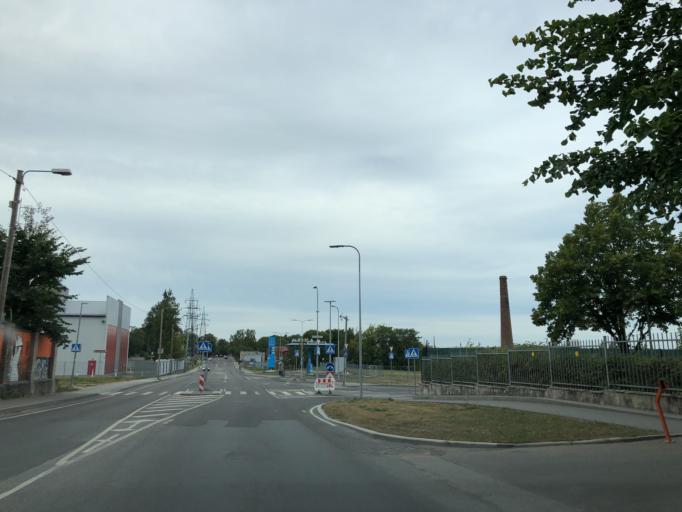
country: EE
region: Harju
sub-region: Tallinna linn
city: Tallinn
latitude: 59.4503
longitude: 24.7230
